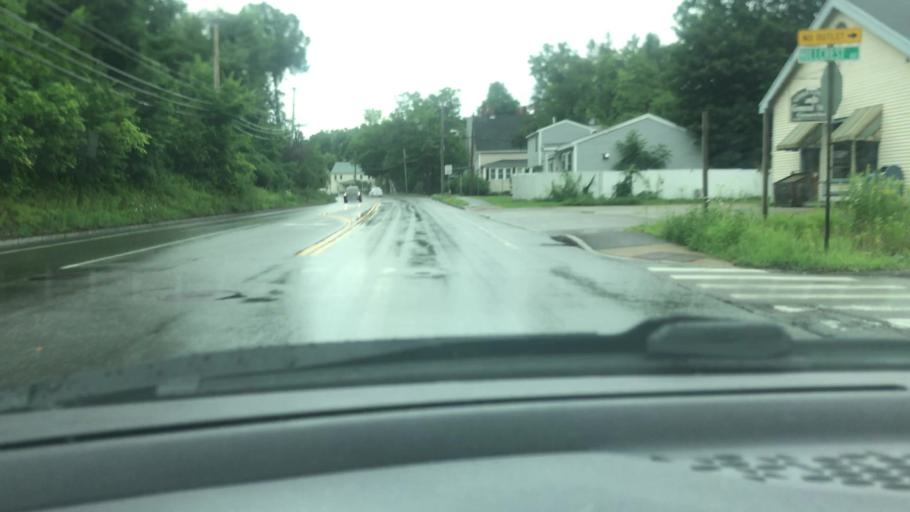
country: US
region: New Hampshire
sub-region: Merrimack County
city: East Concord
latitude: 43.2387
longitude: -71.5654
